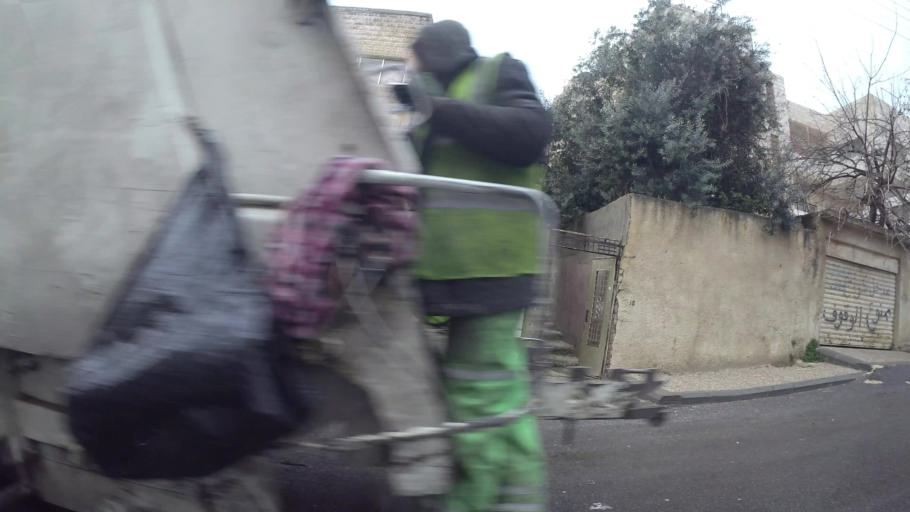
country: JO
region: Amman
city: Al Jubayhah
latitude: 32.0222
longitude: 35.8386
